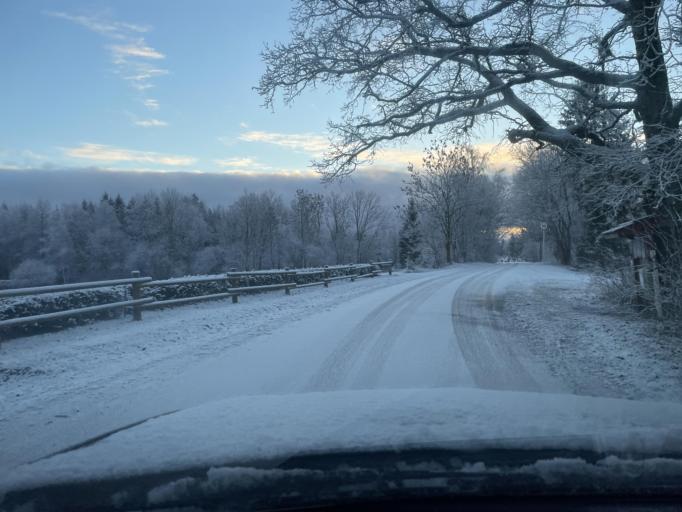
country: EE
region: Harju
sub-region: Keila linn
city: Keila
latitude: 59.3131
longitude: 24.2745
